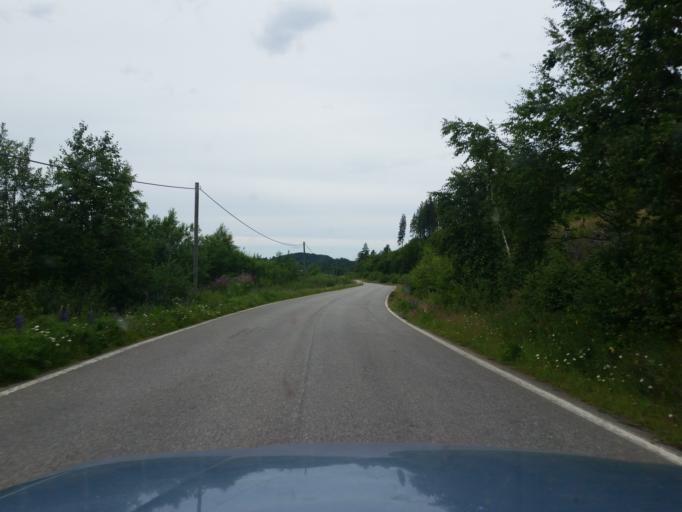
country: FI
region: Uusimaa
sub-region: Helsinki
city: Sammatti
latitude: 60.4492
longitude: 23.8452
